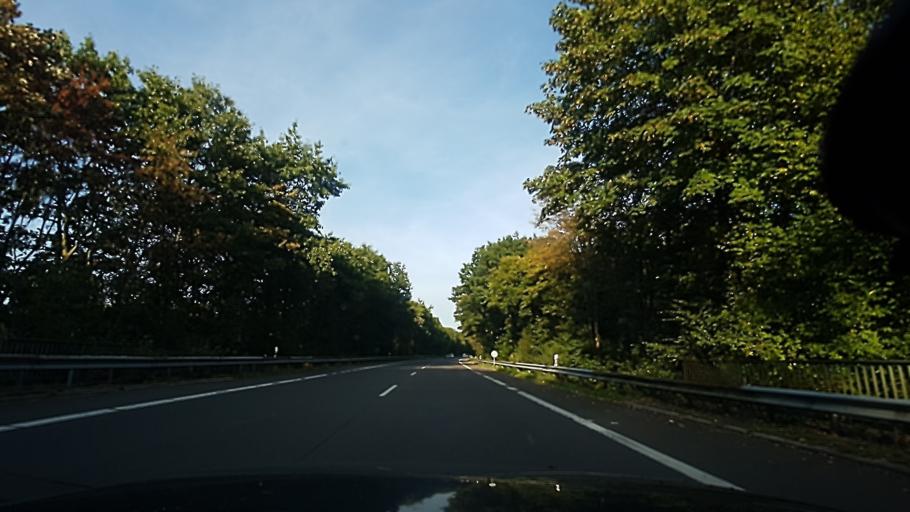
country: DE
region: North Rhine-Westphalia
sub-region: Regierungsbezirk Koln
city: Marienheide
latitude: 51.0681
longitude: 7.5637
